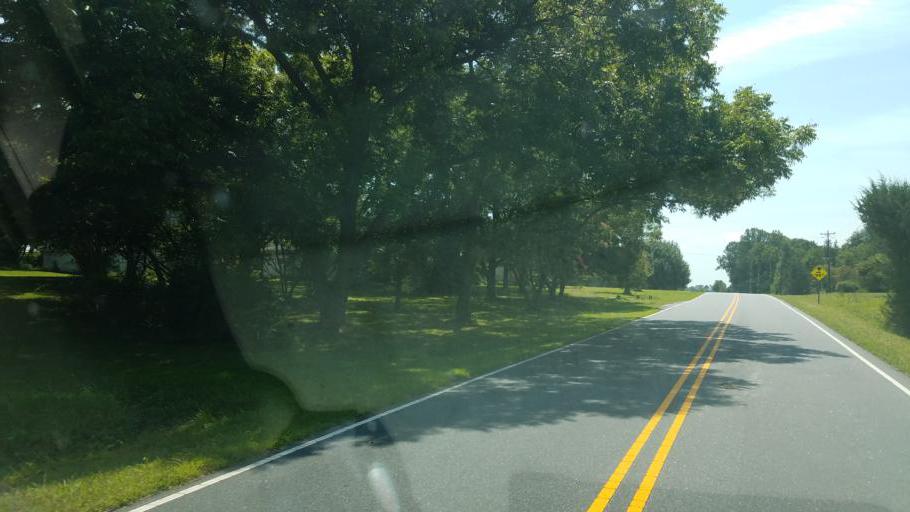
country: US
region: North Carolina
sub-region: Gaston County
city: Cherryville
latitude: 35.5217
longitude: -81.4852
